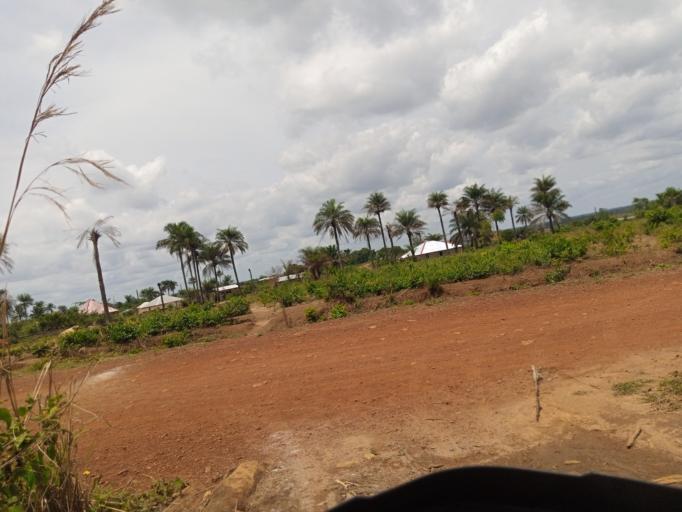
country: SL
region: Western Area
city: Waterloo
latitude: 8.3274
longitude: -13.0002
